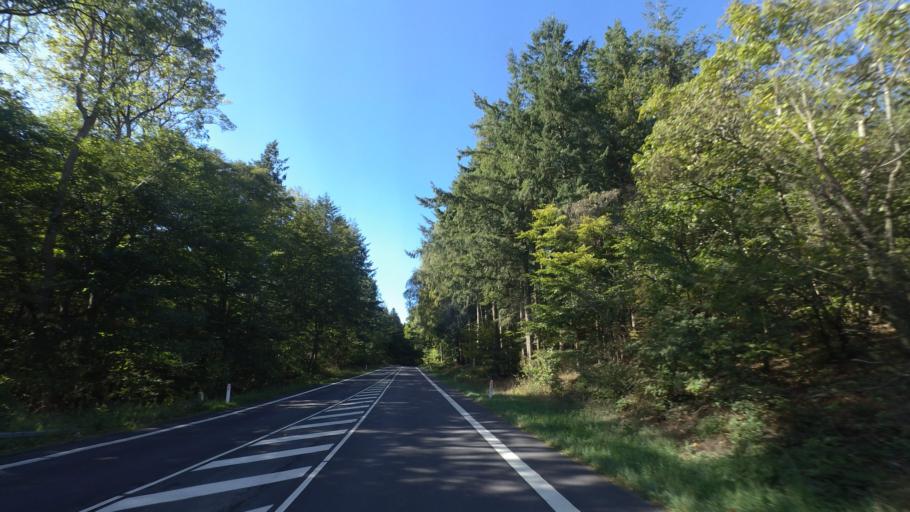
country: DK
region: Capital Region
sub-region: Bornholm Kommune
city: Akirkeby
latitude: 55.0649
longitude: 15.0181
